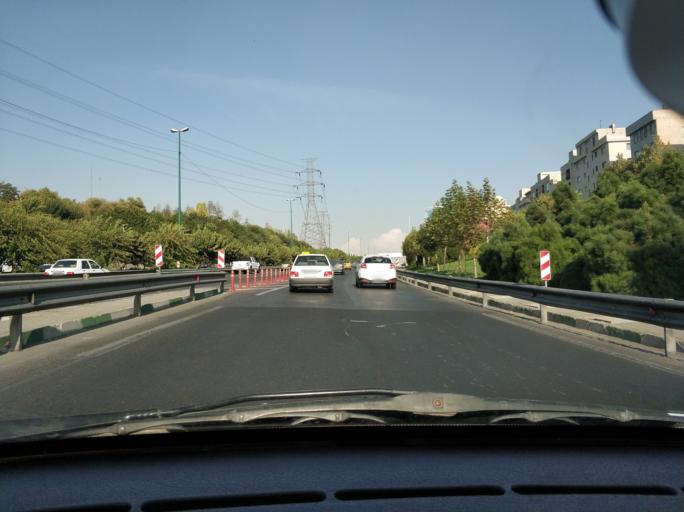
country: IR
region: Tehran
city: Tehran
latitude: 35.7405
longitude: 51.3727
